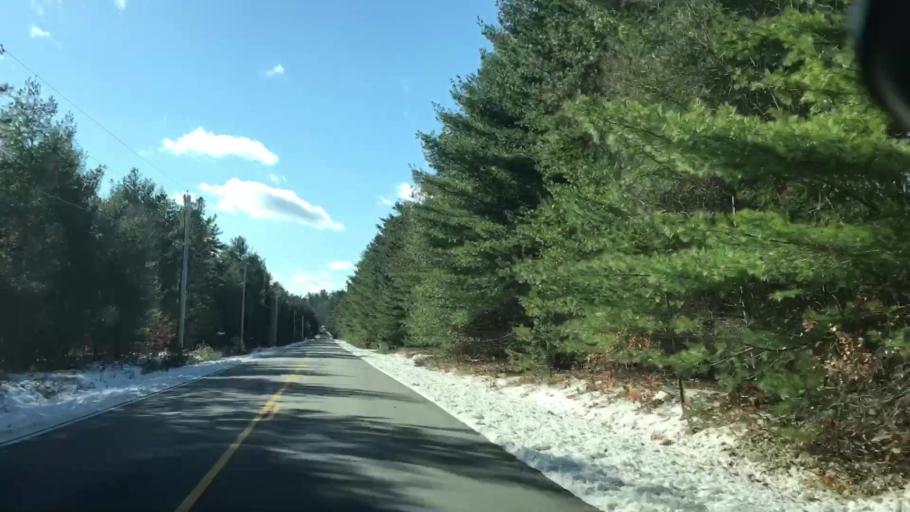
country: US
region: Maine
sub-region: Oxford County
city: Brownfield
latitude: 43.9021
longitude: -70.8860
